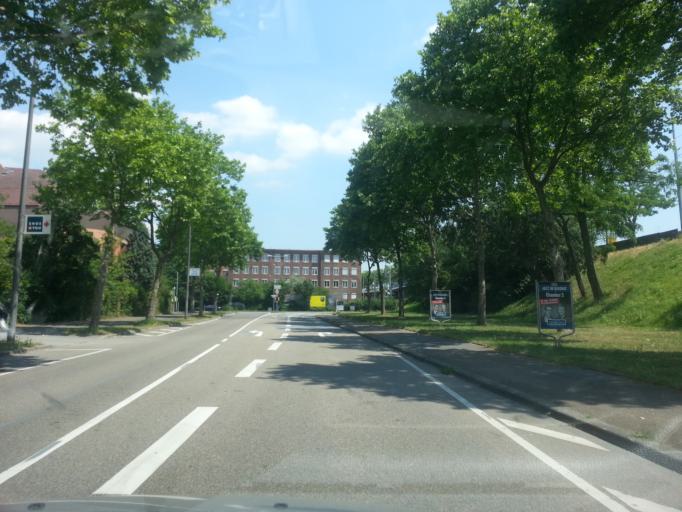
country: DE
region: Baden-Wuerttemberg
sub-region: Karlsruhe Region
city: Mannheim
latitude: 49.5044
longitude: 8.4995
